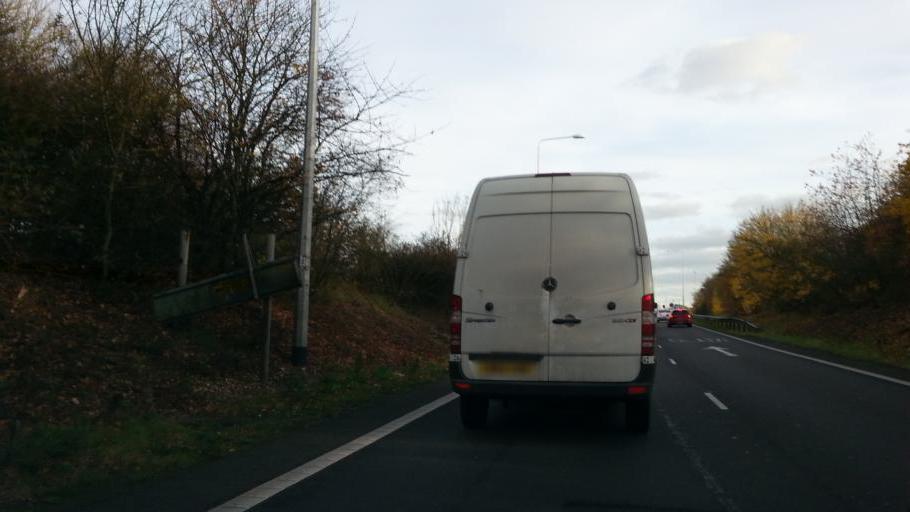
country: GB
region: England
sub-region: Hertfordshire
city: Abbots Langley
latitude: 51.7163
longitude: -0.3734
